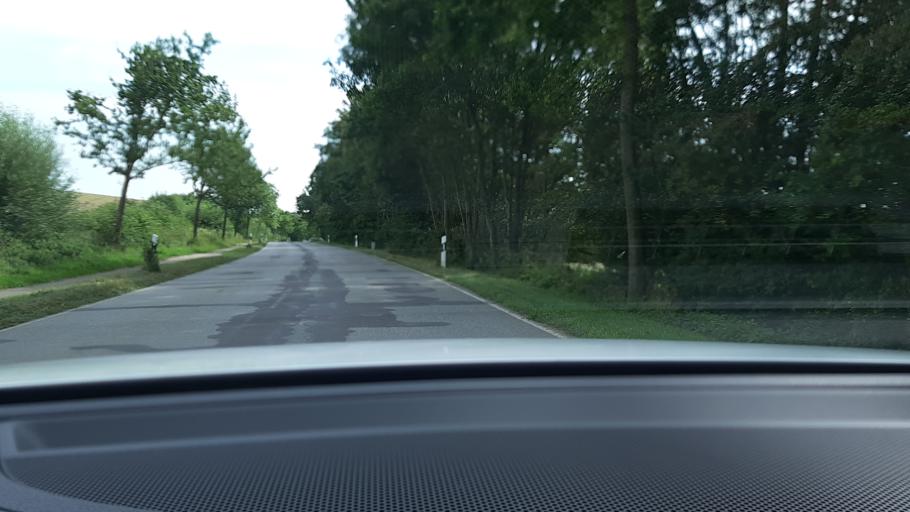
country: DE
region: Schleswig-Holstein
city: Heilshoop
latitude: 53.8937
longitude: 10.5241
